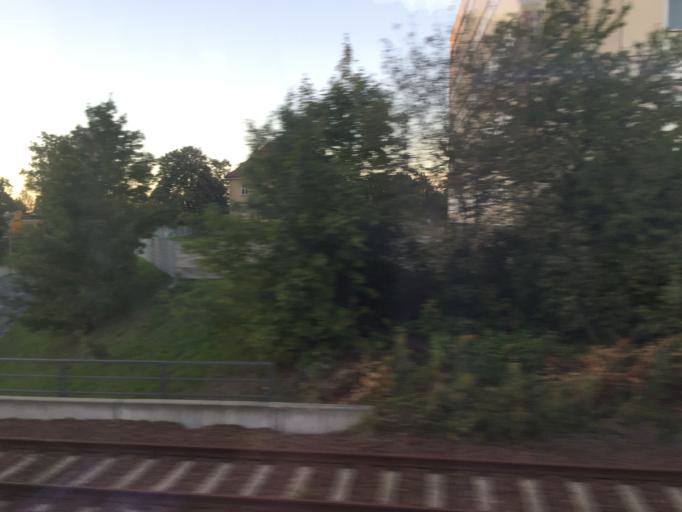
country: DE
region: Saxony
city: Pirna
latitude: 50.9594
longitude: 13.9047
